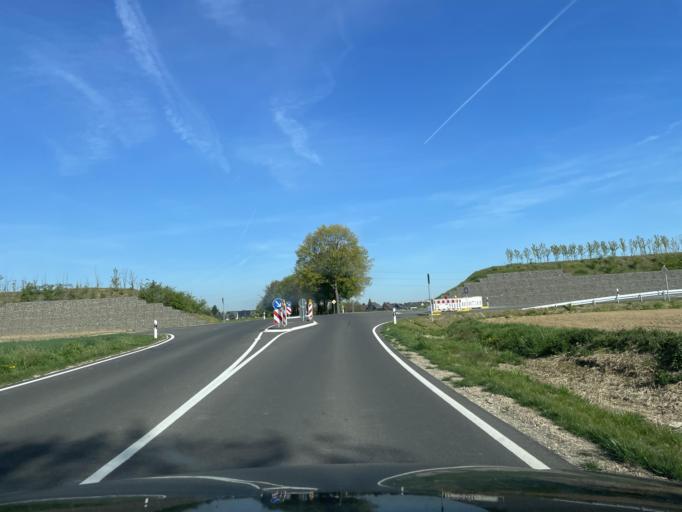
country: DE
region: North Rhine-Westphalia
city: Erkelenz
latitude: 51.0852
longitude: 6.3806
